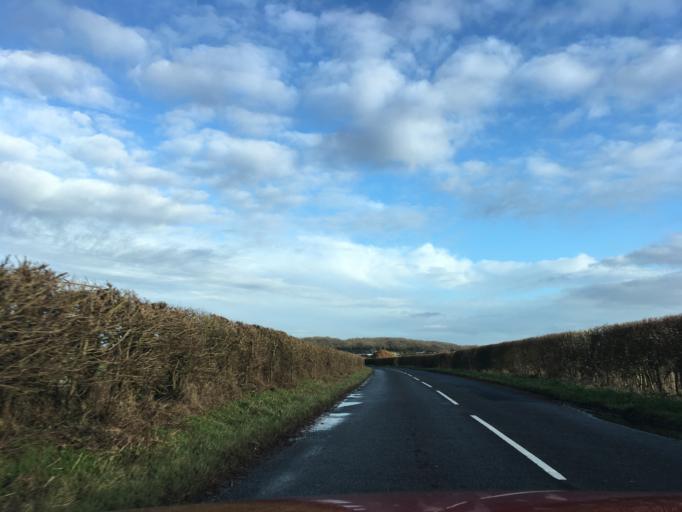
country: GB
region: England
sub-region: Warwickshire
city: Stratford-upon-Avon
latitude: 52.2242
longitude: -1.7512
